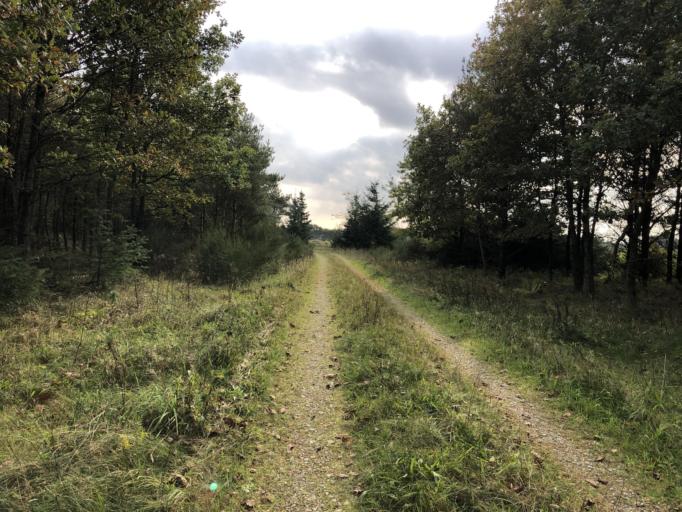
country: DK
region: Central Jutland
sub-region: Holstebro Kommune
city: Ulfborg
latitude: 56.2185
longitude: 8.4358
